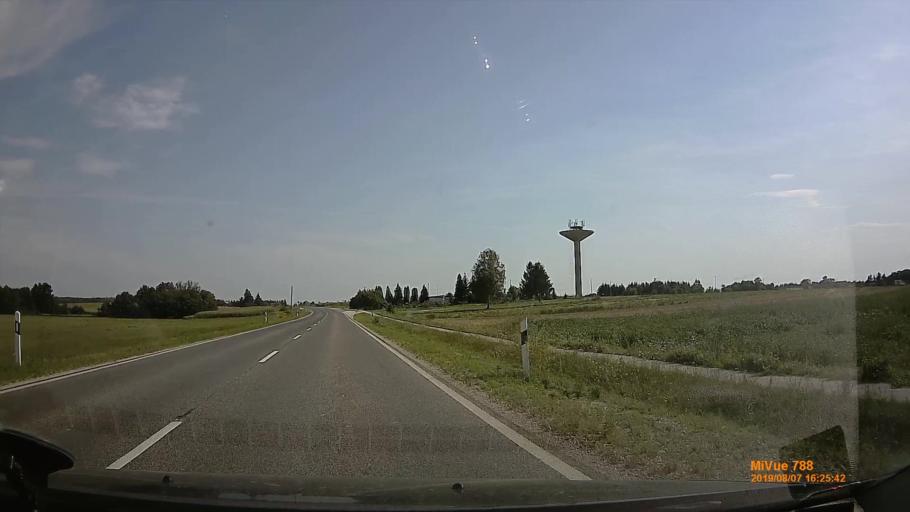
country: HU
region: Zala
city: Lenti
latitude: 46.7193
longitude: 16.5500
